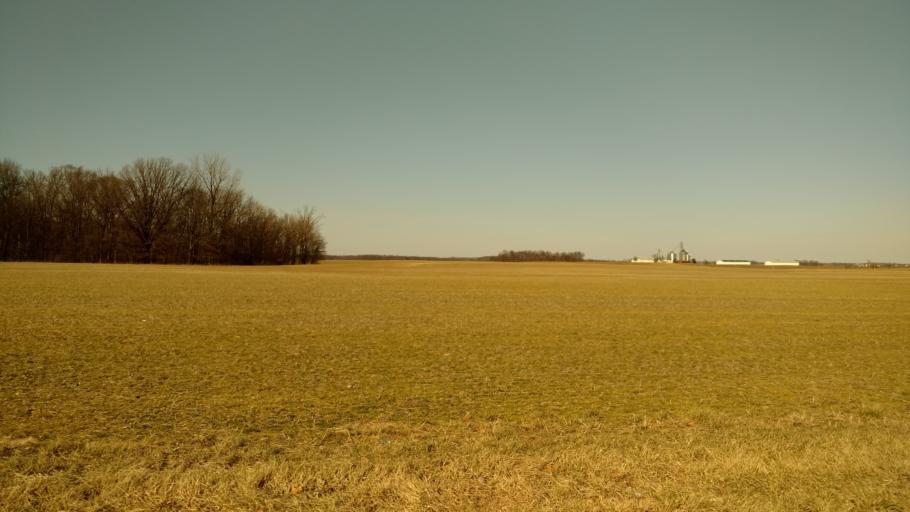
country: US
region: Ohio
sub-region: Wyandot County
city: Upper Sandusky
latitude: 40.7022
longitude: -83.2152
